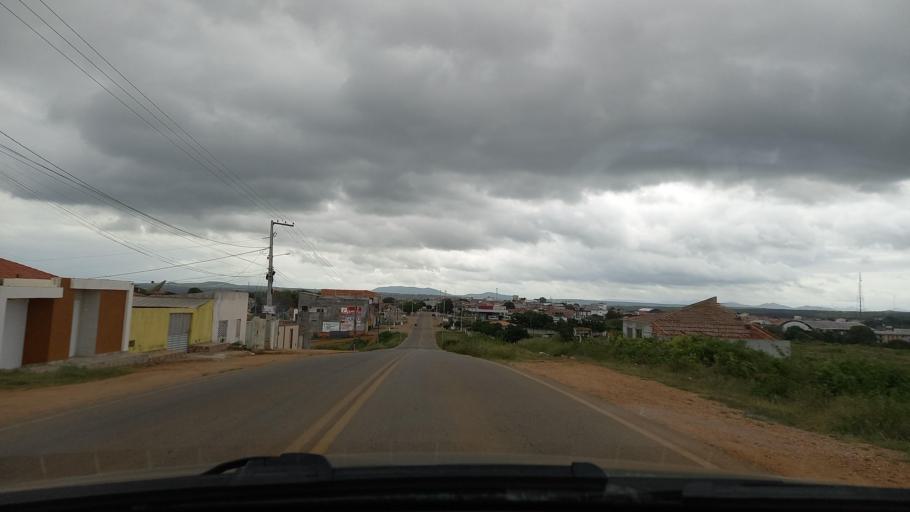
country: BR
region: Sergipe
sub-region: Caninde De Sao Francisco
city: Caninde de Sao Francisco
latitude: -9.6697
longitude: -37.7984
